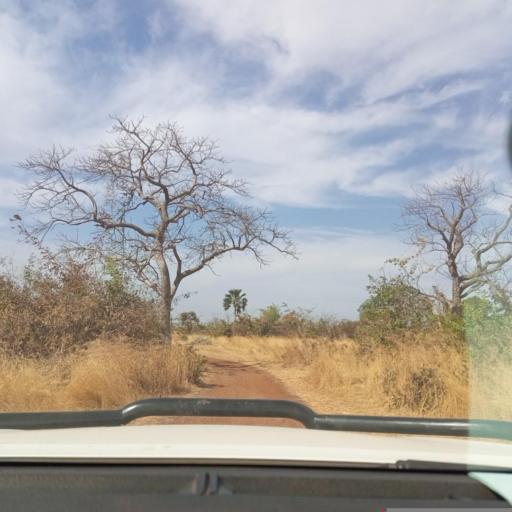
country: ML
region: Koulikoro
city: Kati
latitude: 12.7452
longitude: -8.2495
